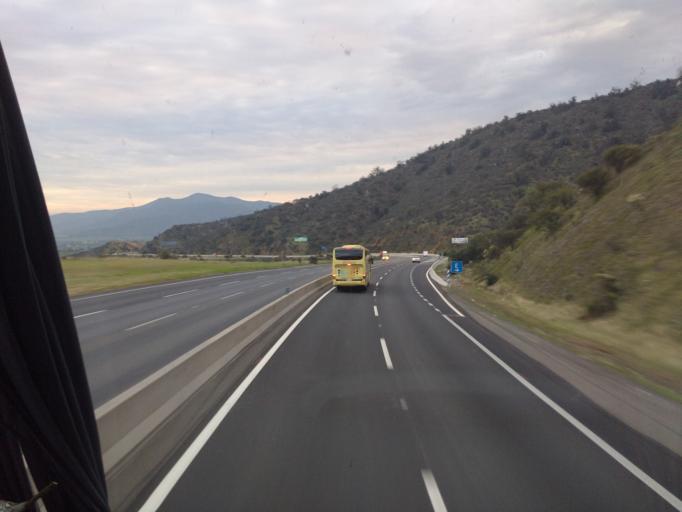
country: CL
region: Santiago Metropolitan
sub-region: Provincia de Chacabuco
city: Lampa
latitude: -33.4411
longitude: -71.0013
